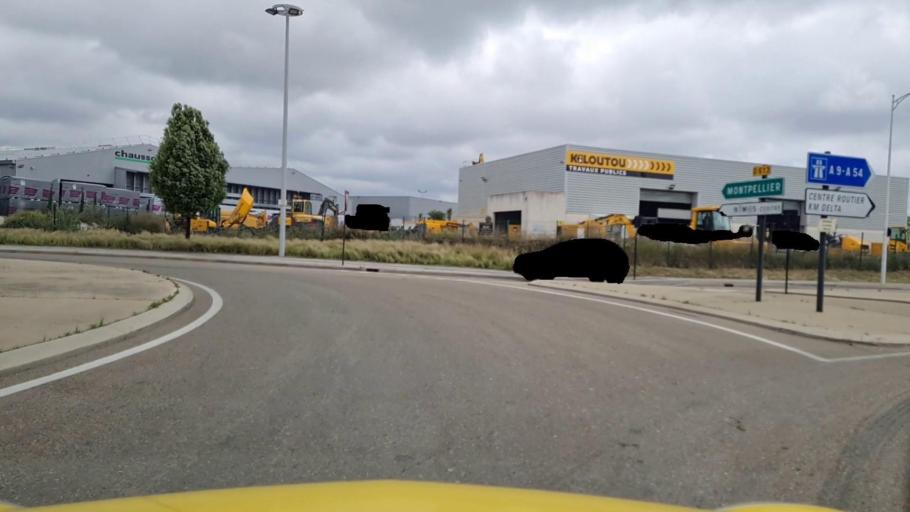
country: FR
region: Languedoc-Roussillon
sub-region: Departement du Gard
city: Milhaud
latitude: 43.8095
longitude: 4.3322
